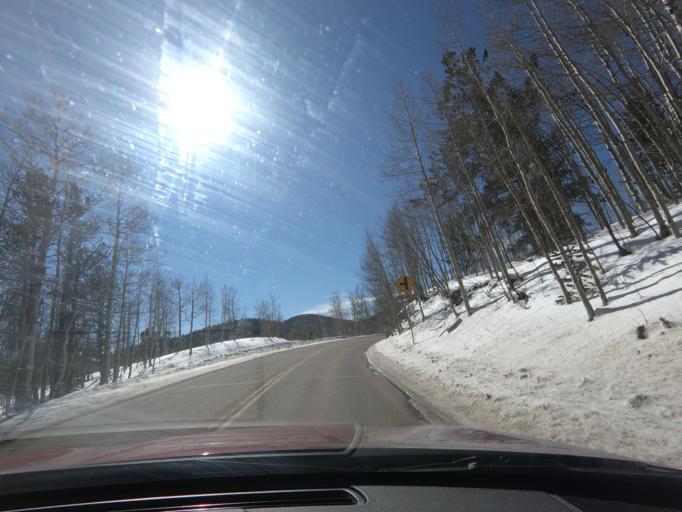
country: US
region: Colorado
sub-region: Teller County
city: Cripple Creek
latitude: 38.7452
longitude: -105.1001
